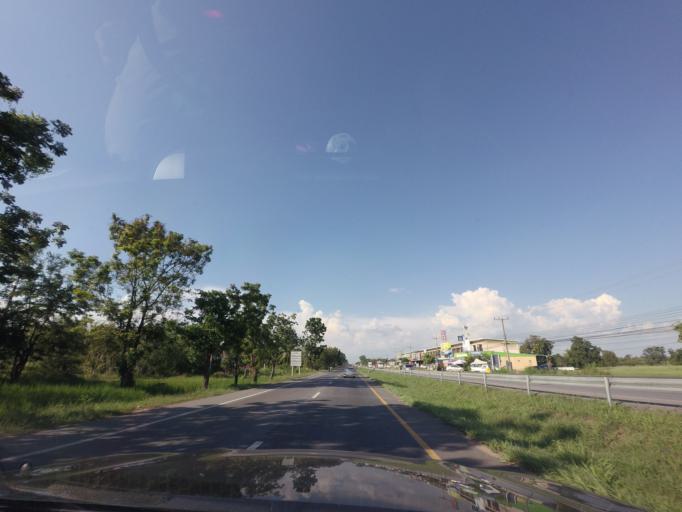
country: TH
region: Khon Kaen
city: Non Sila
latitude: 15.9689
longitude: 102.6922
